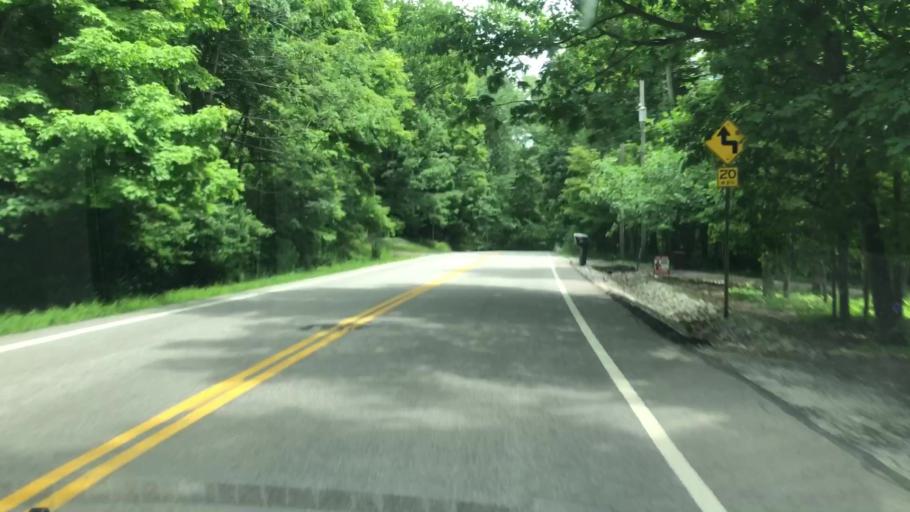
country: US
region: Ohio
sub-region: Summit County
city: Montrose-Ghent
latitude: 41.1696
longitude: -81.6121
